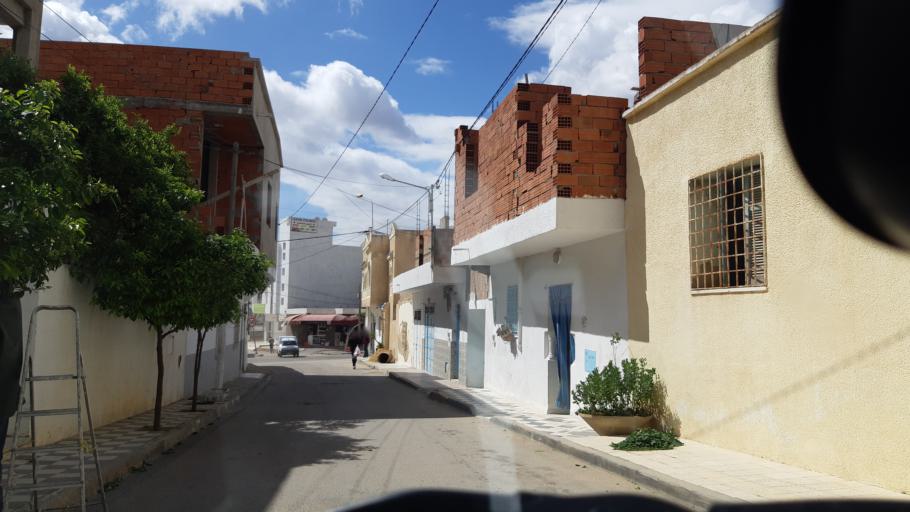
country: TN
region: Susah
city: Akouda
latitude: 35.8769
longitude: 10.5400
